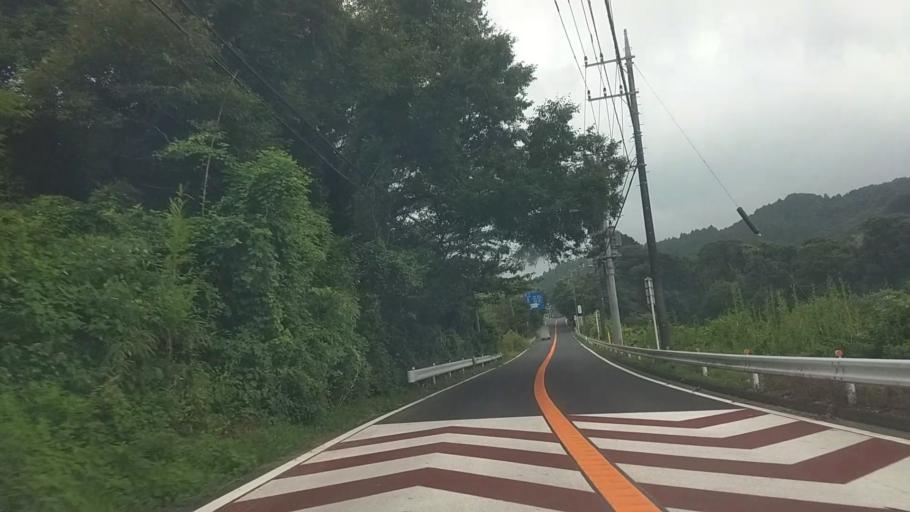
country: JP
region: Chiba
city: Kawaguchi
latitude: 35.2081
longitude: 140.0705
